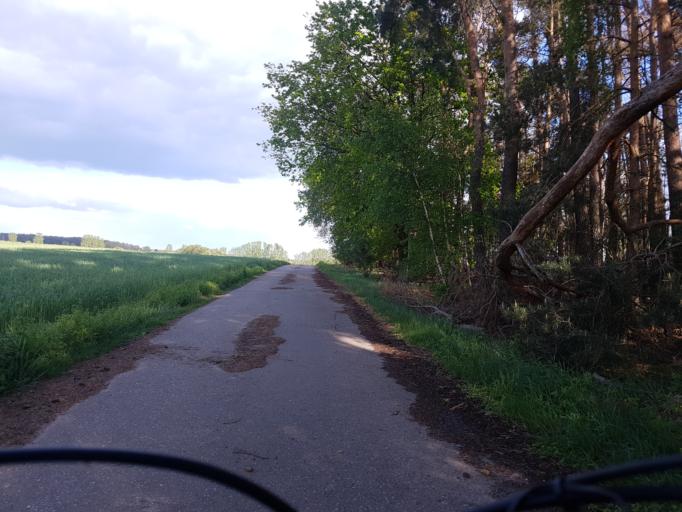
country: DE
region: Brandenburg
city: Schilda
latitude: 51.5629
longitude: 13.3955
